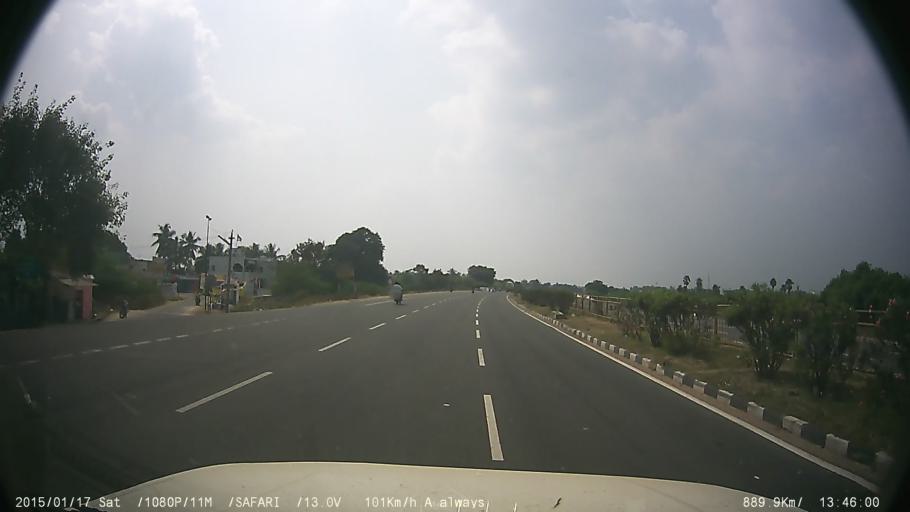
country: IN
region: Tamil Nadu
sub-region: Vellore
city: Vellore
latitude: 12.9153
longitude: 79.0867
